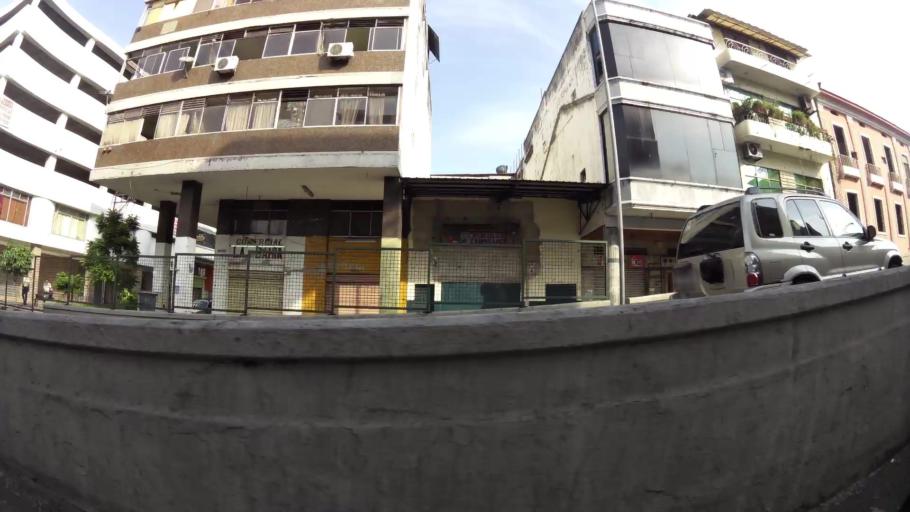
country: EC
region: Guayas
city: Guayaquil
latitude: -2.2003
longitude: -79.8849
